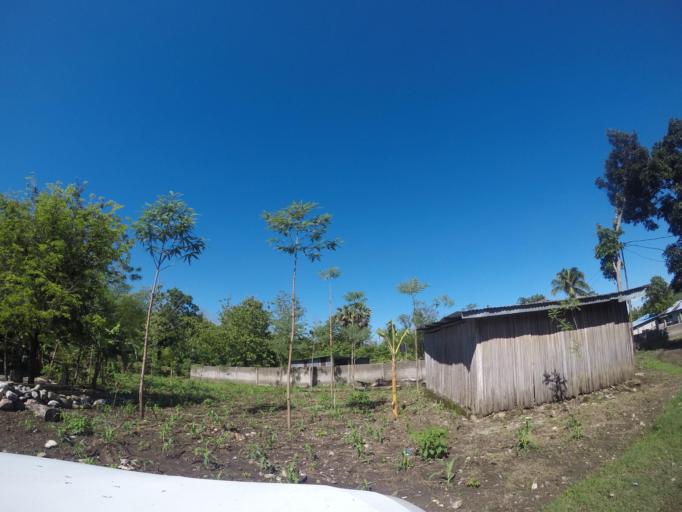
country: TL
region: Bobonaro
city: Maliana
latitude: -8.9933
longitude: 125.2132
